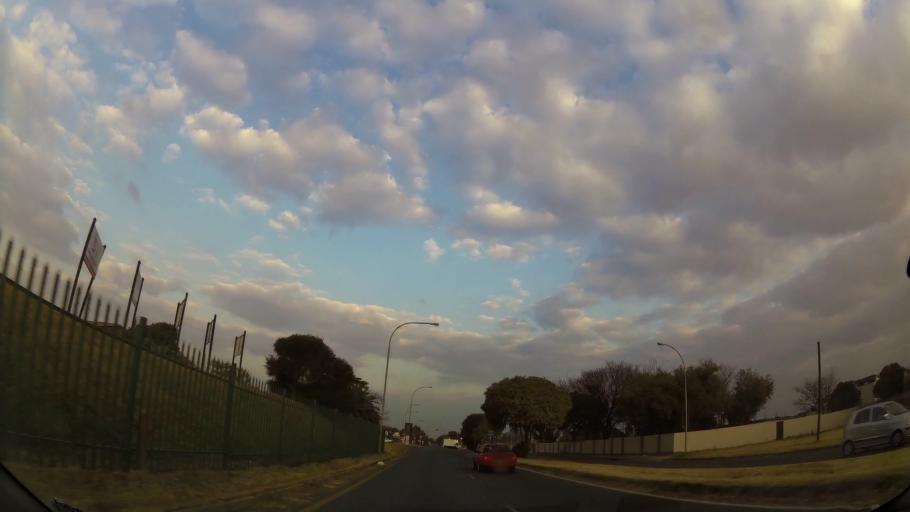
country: ZA
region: Gauteng
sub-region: Ekurhuleni Metropolitan Municipality
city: Benoni
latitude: -26.1657
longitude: 28.3082
